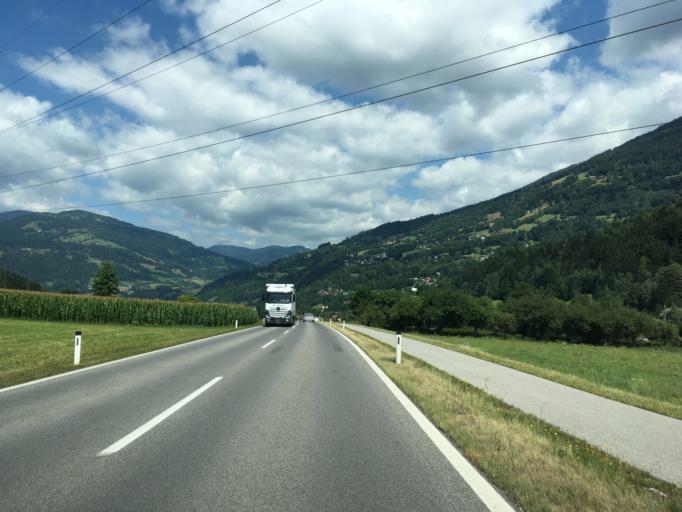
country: AT
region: Carinthia
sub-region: Politischer Bezirk Villach Land
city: Feld am See
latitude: 46.7840
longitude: 13.7376
